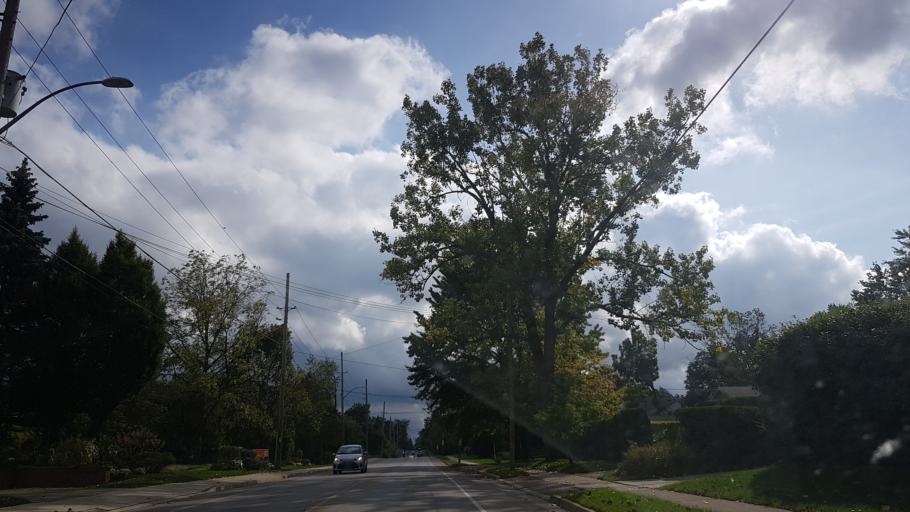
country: CA
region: Ontario
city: London
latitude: 42.9563
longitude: -81.2415
